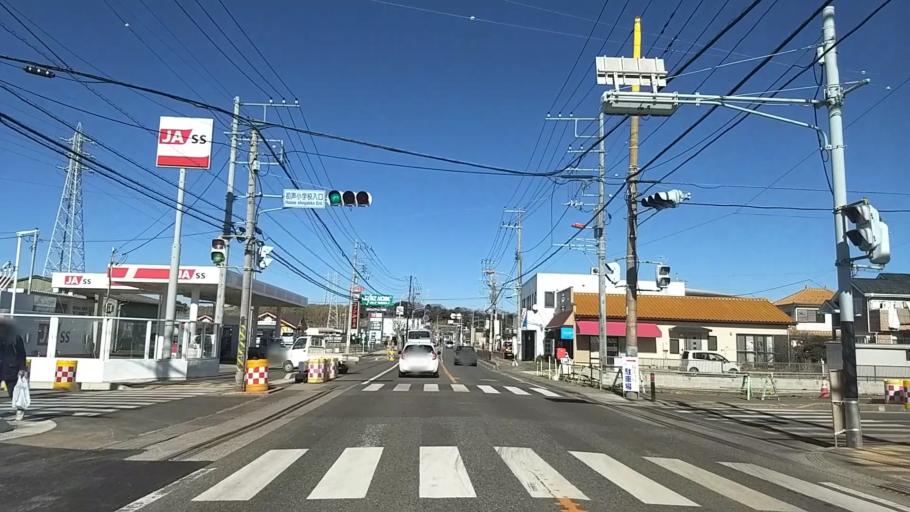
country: JP
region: Kanagawa
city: Miura
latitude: 35.1855
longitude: 139.6288
